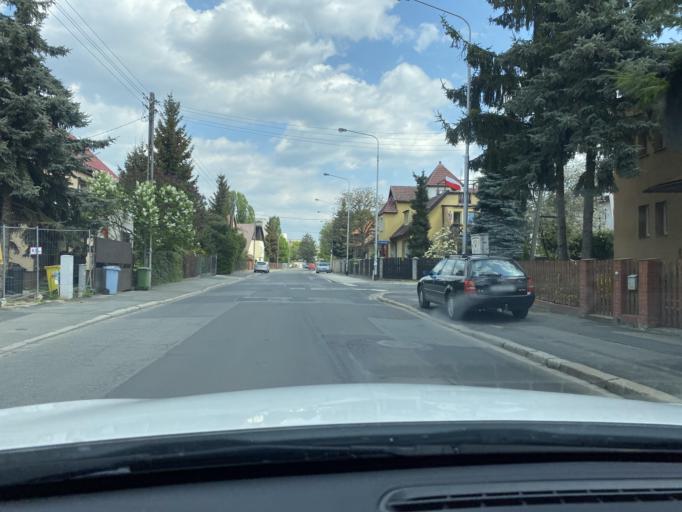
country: PL
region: Lower Silesian Voivodeship
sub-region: Powiat wroclawski
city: Wroclaw
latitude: 51.1376
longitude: 17.0183
